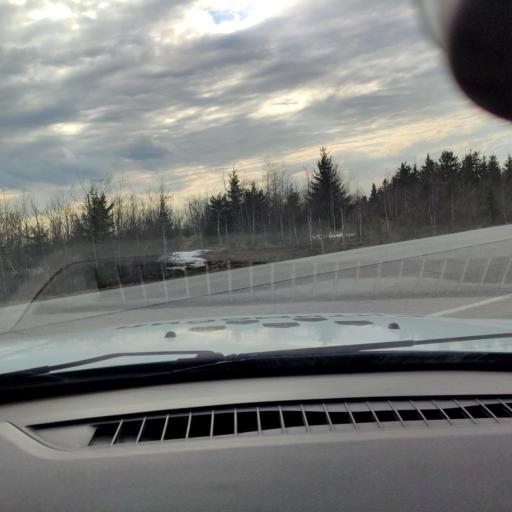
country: RU
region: Perm
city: Gremyachinsk
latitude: 58.5817
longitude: 57.7706
